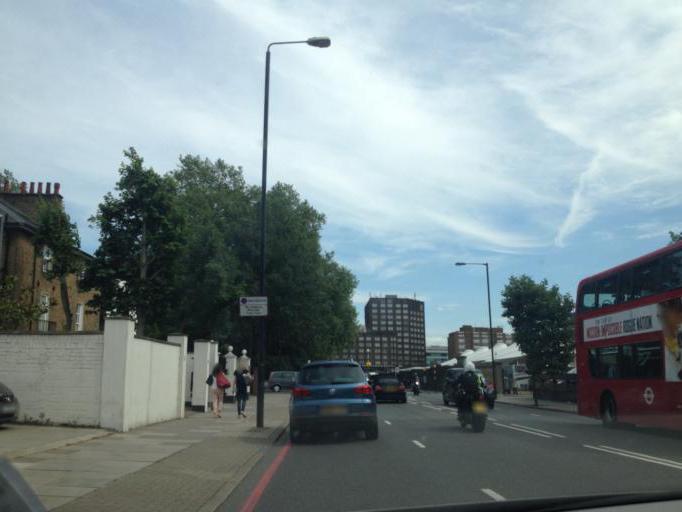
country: GB
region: England
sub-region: Greater London
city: Belsize Park
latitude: 51.5320
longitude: -0.1713
